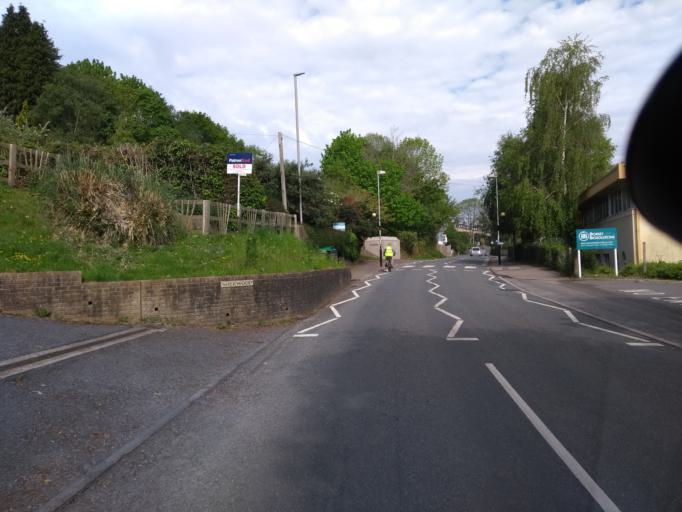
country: GB
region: England
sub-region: Dorset
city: Lyme Regis
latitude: 50.7293
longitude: -2.9464
